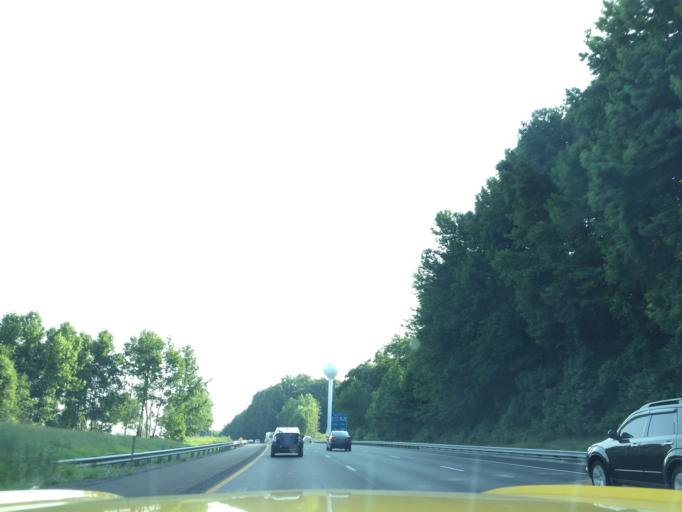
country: US
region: Maryland
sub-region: Harford County
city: Riverside
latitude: 39.5002
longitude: -76.2302
